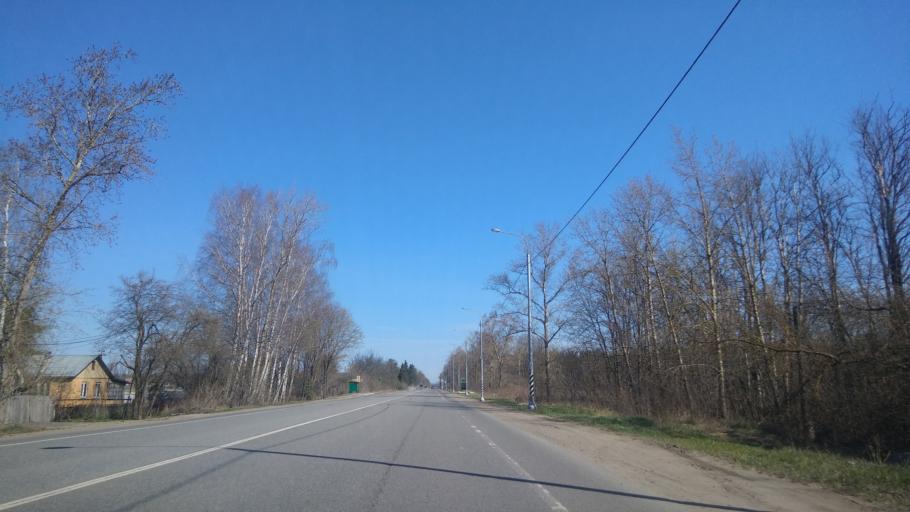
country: RU
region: Moskovskaya
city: Pushkino
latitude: 56.0246
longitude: 37.8713
